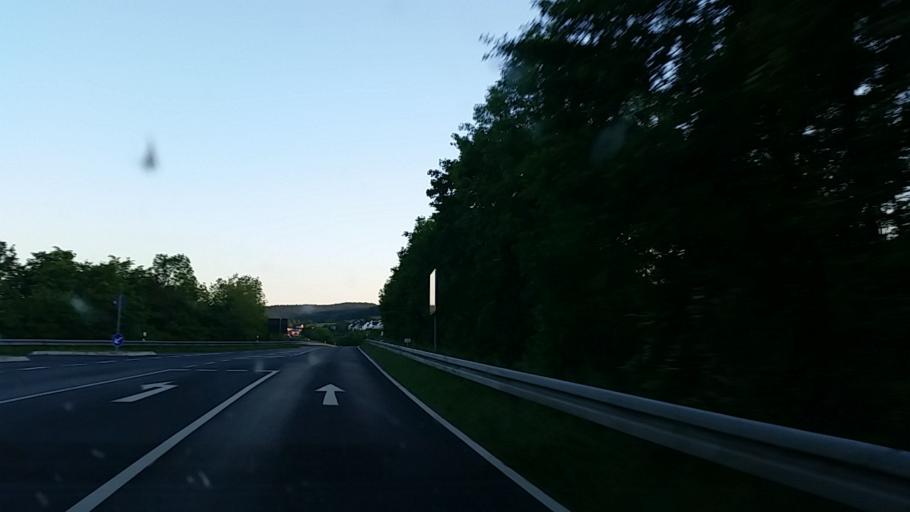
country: DE
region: Bavaria
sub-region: Regierungsbezirk Unterfranken
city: Burgsinn
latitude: 50.1594
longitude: 9.6536
